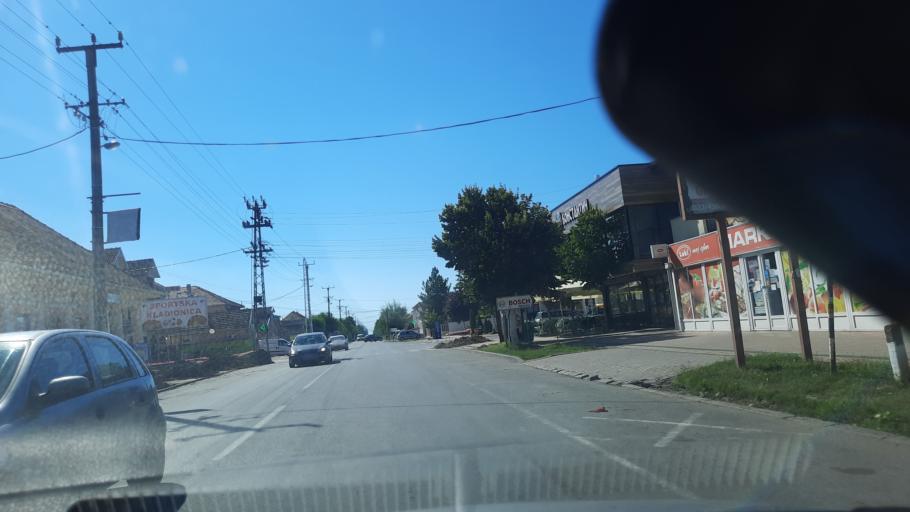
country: RS
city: Simanovci
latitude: 44.8744
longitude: 20.0897
